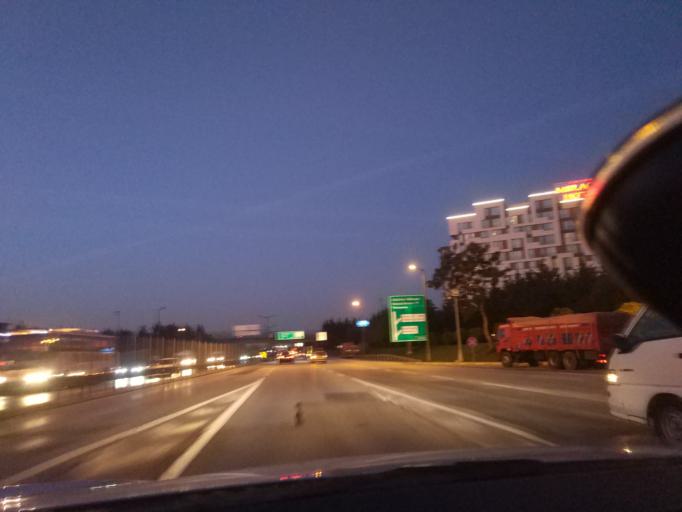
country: TR
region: Istanbul
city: Sultanbeyli
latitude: 40.9326
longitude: 29.3300
